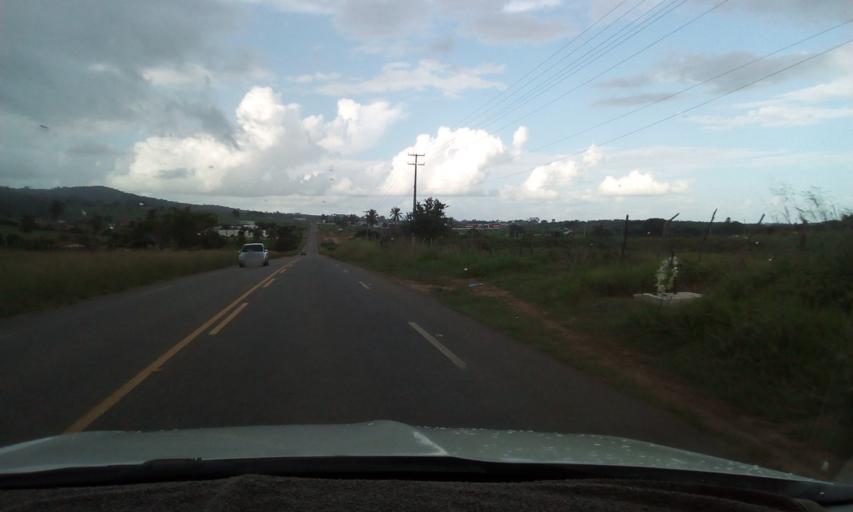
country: BR
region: Paraiba
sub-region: Guarabira
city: Guarabira
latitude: -6.8611
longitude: -35.4801
